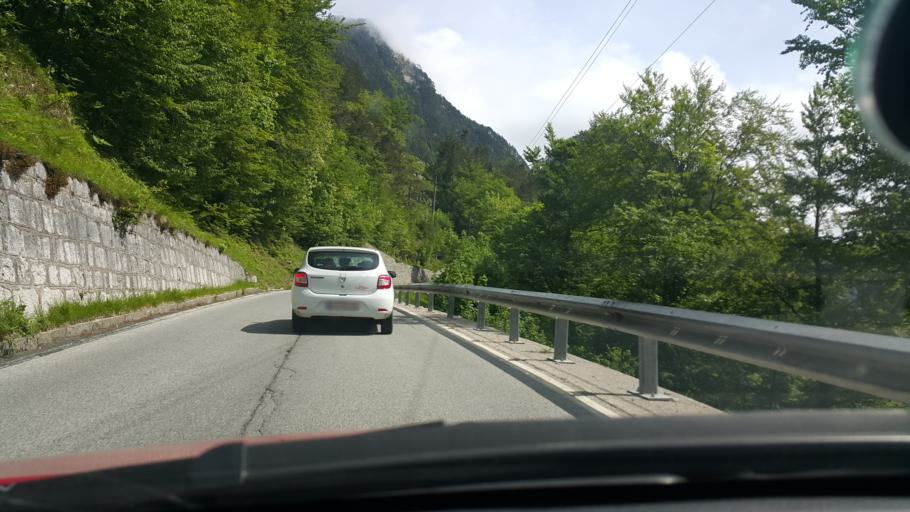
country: AT
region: Carinthia
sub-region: Politischer Bezirk Klagenfurt Land
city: Ferlach
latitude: 46.4833
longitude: 14.2616
